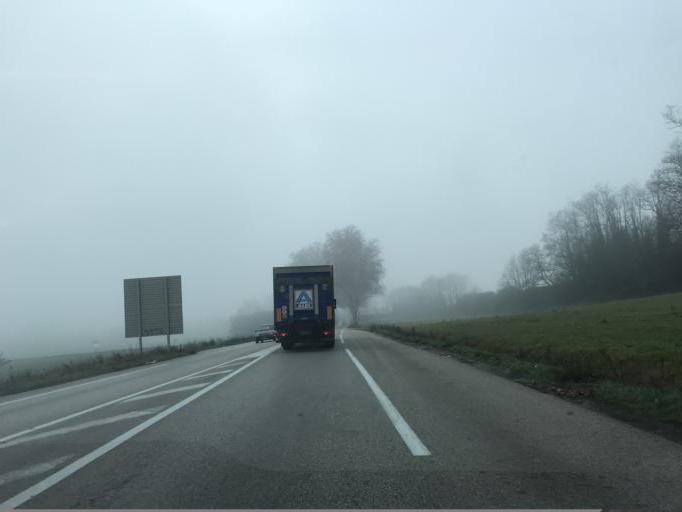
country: FR
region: Rhone-Alpes
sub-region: Departement de l'Ain
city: Mionnay
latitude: 45.8792
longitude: 4.9104
